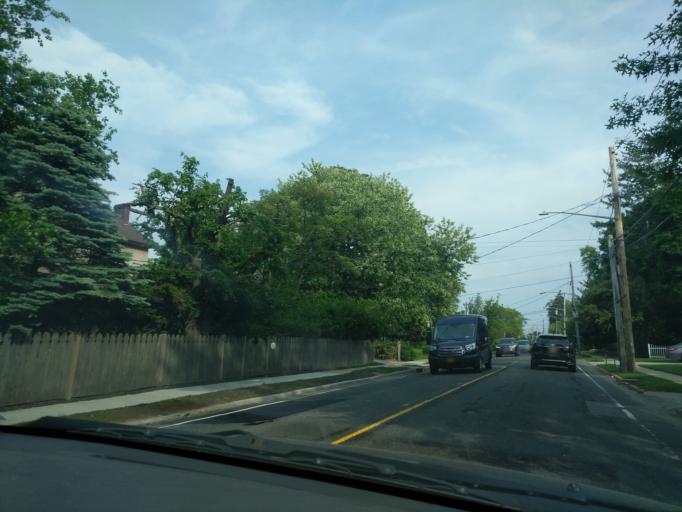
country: US
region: New York
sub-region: Nassau County
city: Rockville Centre
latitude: 40.6529
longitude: -73.6450
